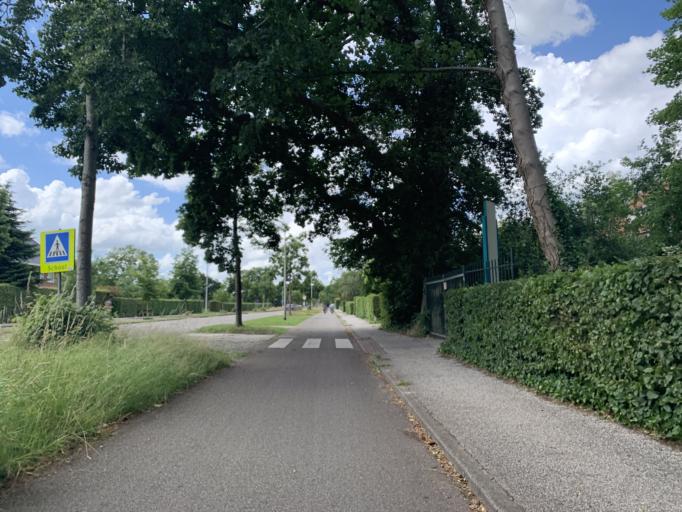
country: NL
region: Groningen
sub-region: Gemeente Haren
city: Haren
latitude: 53.1845
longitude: 6.5894
